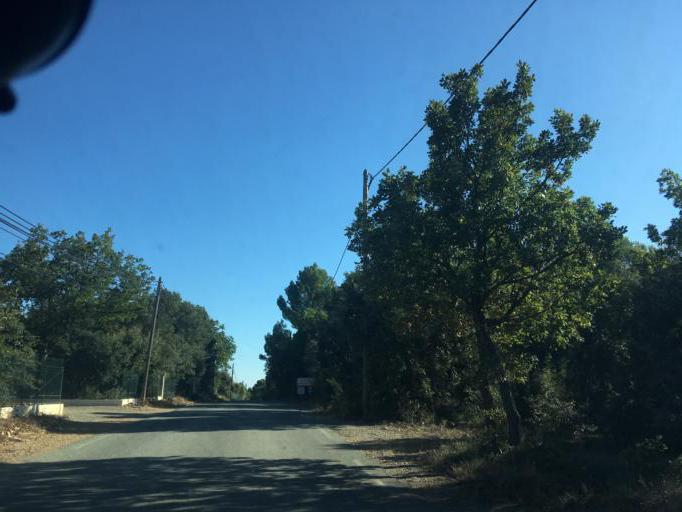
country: FR
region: Provence-Alpes-Cote d'Azur
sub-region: Departement du Var
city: Regusse
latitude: 43.6582
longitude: 6.1614
